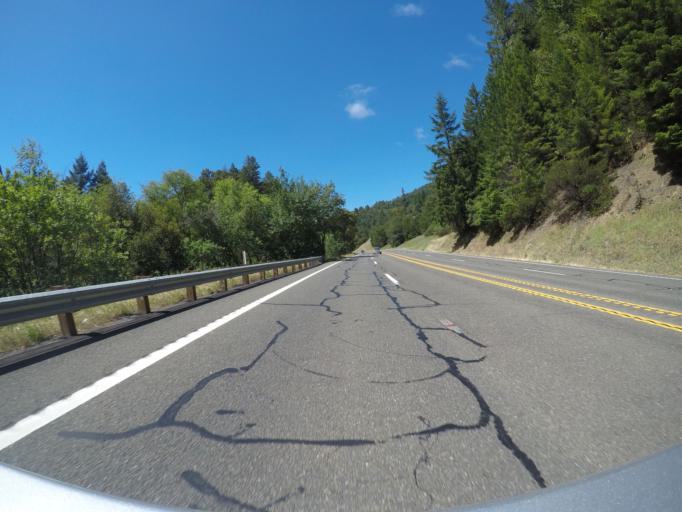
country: US
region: California
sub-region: Mendocino County
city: Laytonville
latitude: 39.5657
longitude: -123.4350
